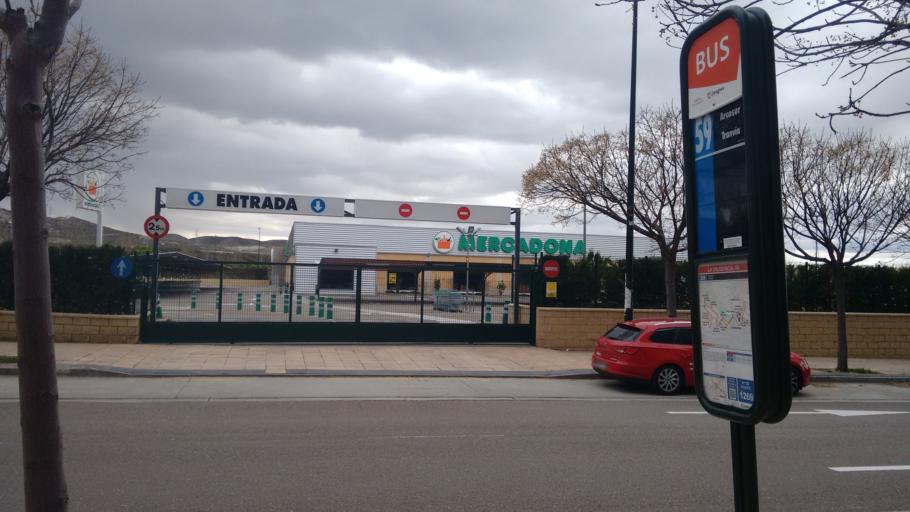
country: ES
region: Aragon
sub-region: Provincia de Zaragoza
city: Montecanal
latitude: 41.6231
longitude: -0.9361
